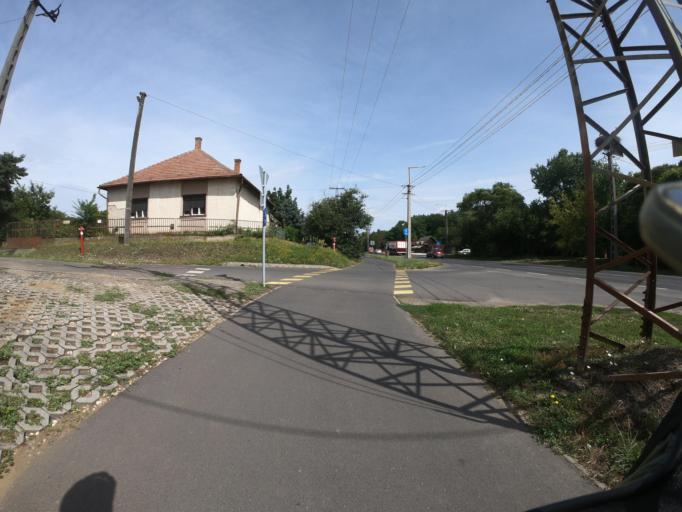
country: HU
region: Jasz-Nagykun-Szolnok
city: Tiszafured
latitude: 47.6142
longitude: 20.7489
